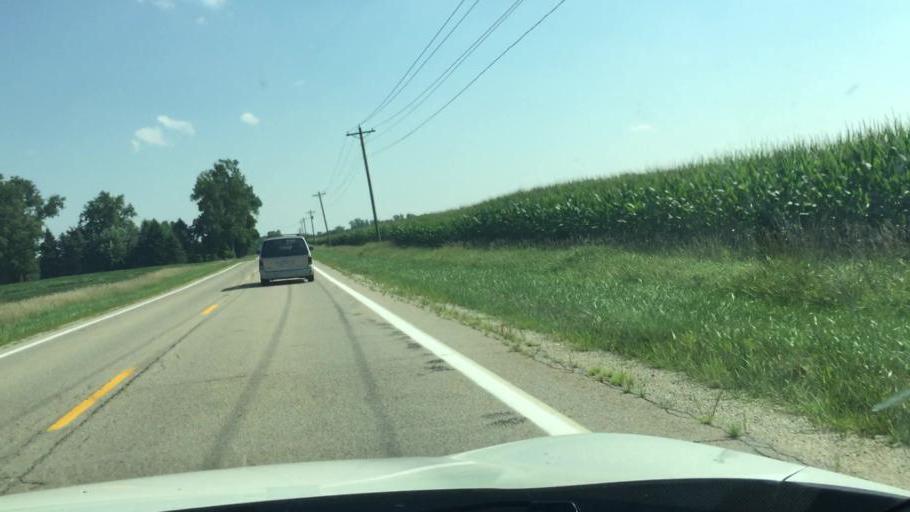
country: US
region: Ohio
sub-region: Champaign County
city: Mechanicsburg
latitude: 40.1317
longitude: -83.5312
